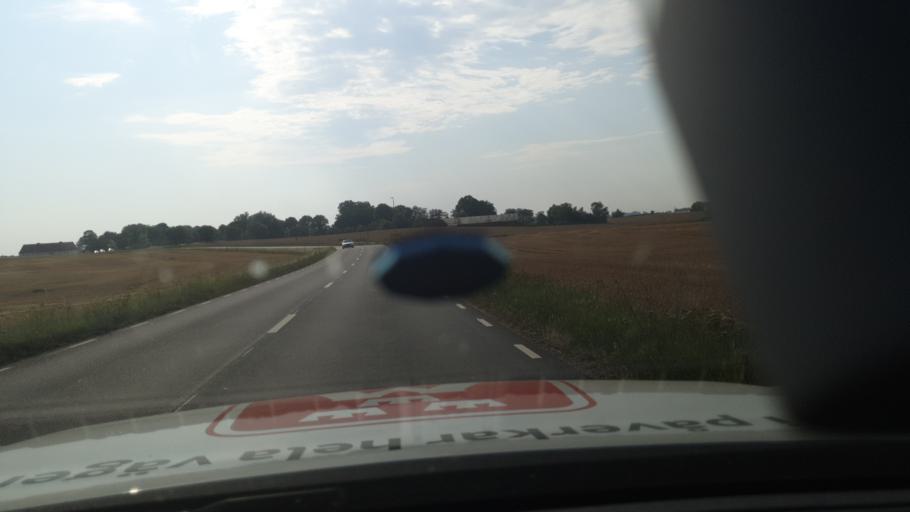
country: SE
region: Skane
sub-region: Svedala Kommun
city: Svedala
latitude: 55.4541
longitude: 13.2019
